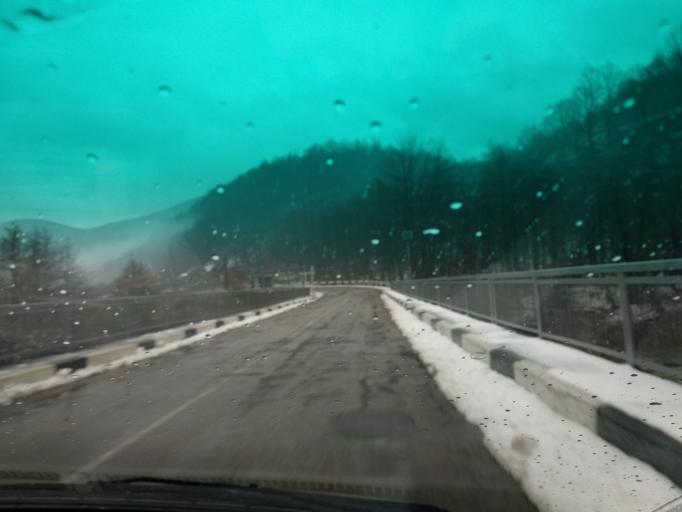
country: RU
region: Krasnodarskiy
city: Khadyzhensk
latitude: 44.2350
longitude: 39.3787
